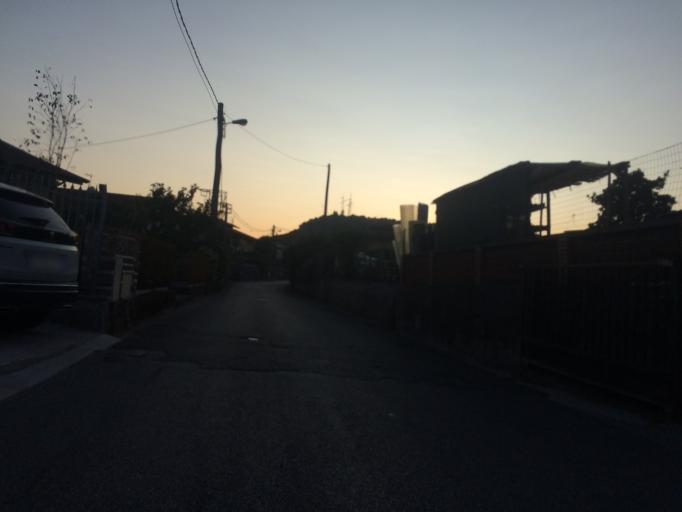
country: IT
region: Tuscany
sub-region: Provincia di Massa-Carrara
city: Massa
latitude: 44.0425
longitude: 10.1079
